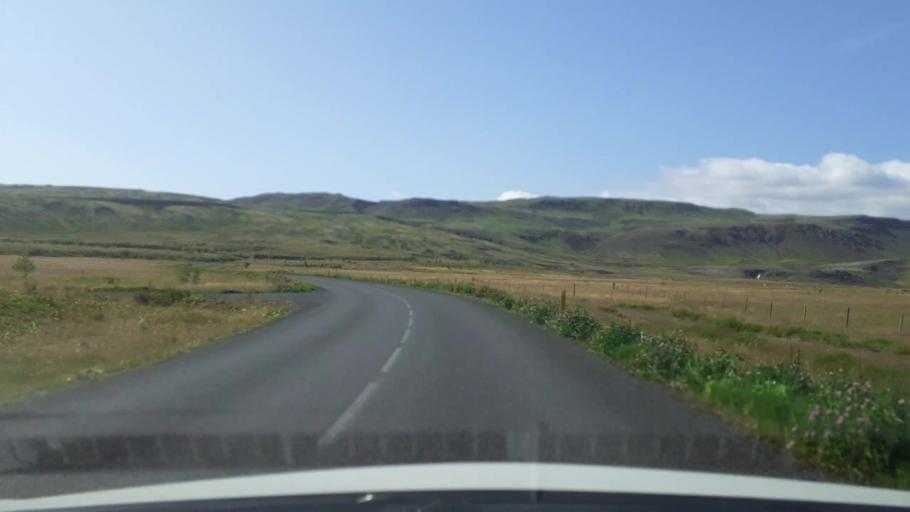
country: IS
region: South
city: Hveragerdi
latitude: 64.0130
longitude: -21.1964
